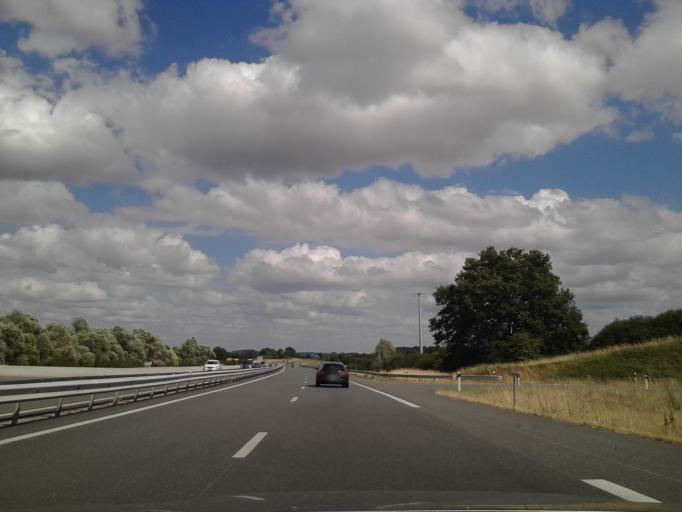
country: FR
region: Centre
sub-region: Departement du Cher
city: Orval
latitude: 46.7237
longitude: 2.4393
